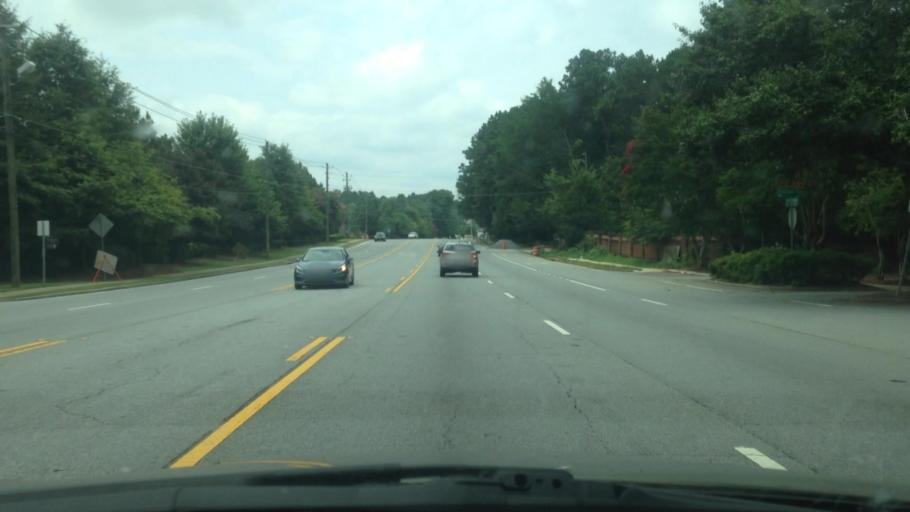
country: US
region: Georgia
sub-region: DeKalb County
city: Tucker
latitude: 33.8688
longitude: -84.1789
